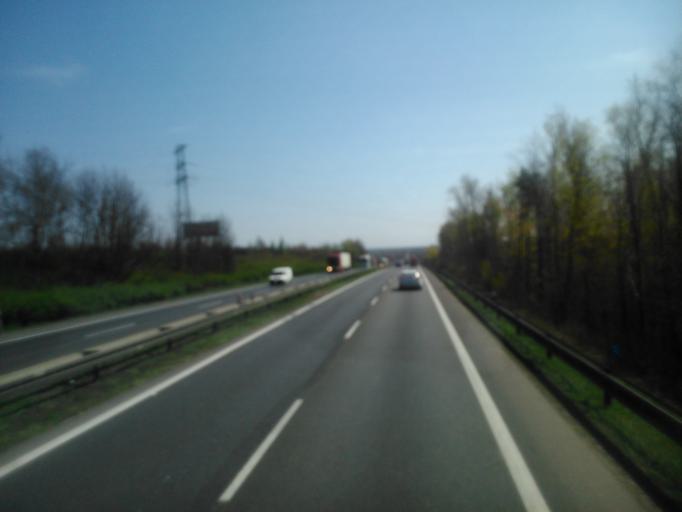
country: PL
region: Silesian Voivodeship
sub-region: Powiat czestochowski
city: Huta Stara B
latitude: 50.7421
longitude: 19.1552
